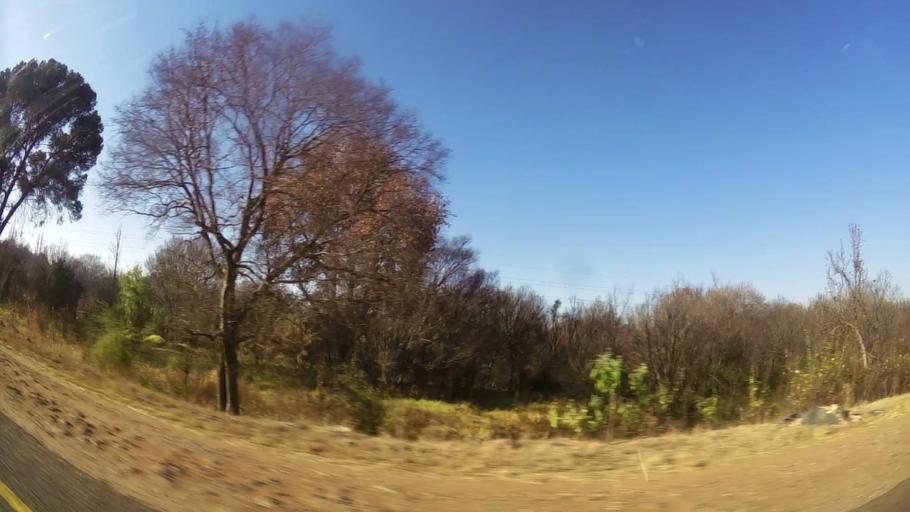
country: ZA
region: Gauteng
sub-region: City of Tshwane Metropolitan Municipality
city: Centurion
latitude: -25.8266
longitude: 28.1556
